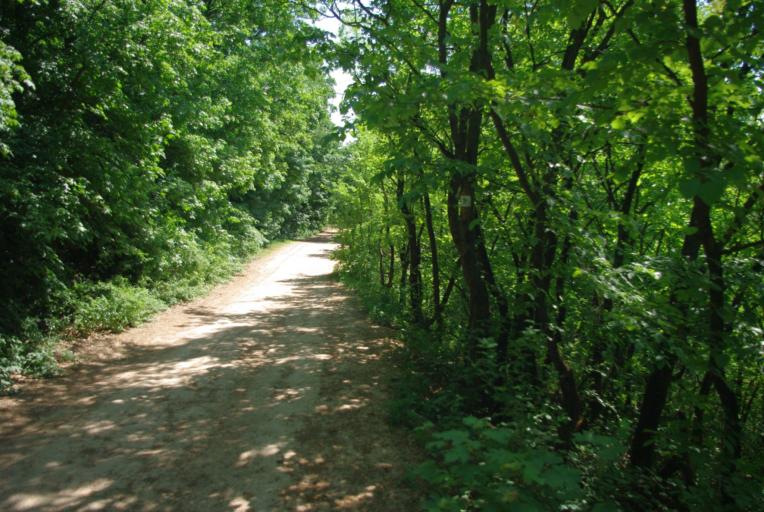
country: HU
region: Pest
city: Pilisborosjeno
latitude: 47.6183
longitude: 18.9761
